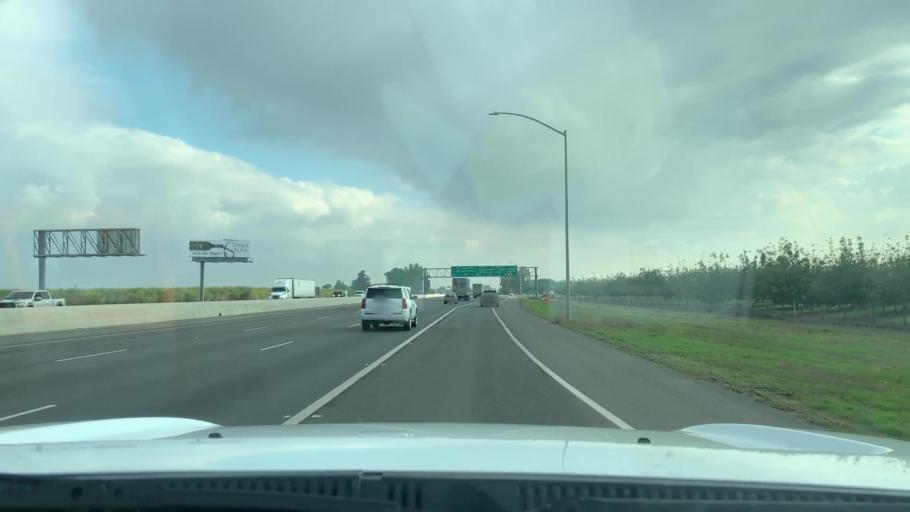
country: US
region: California
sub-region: Tulare County
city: Goshen
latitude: 36.3355
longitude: -119.4148
